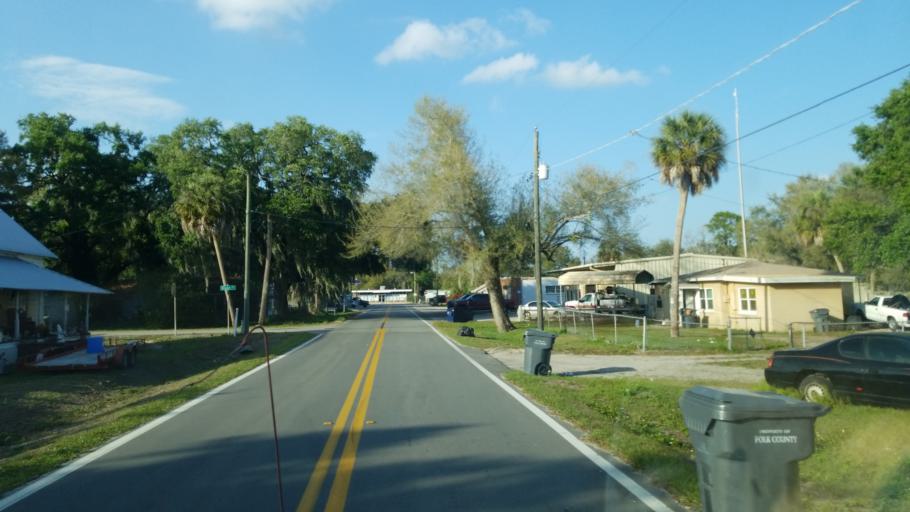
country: US
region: Florida
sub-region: Polk County
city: Mulberry
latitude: 27.7925
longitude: -81.9781
